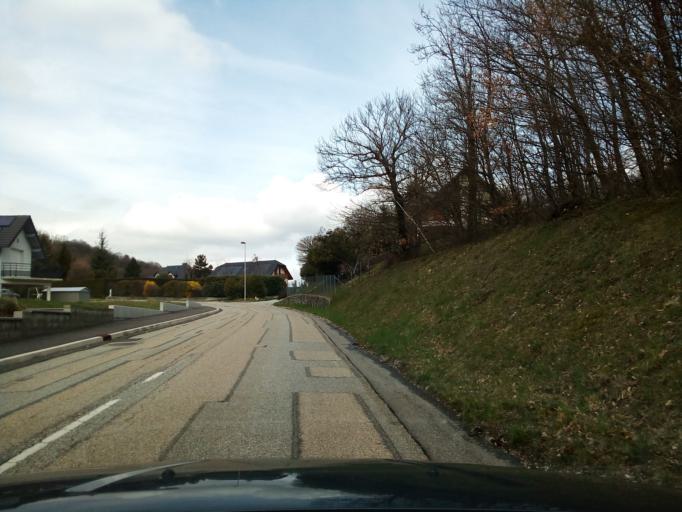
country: FR
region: Rhone-Alpes
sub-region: Departement de la Savoie
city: Saint-Baldoph
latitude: 45.5401
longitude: 5.9490
